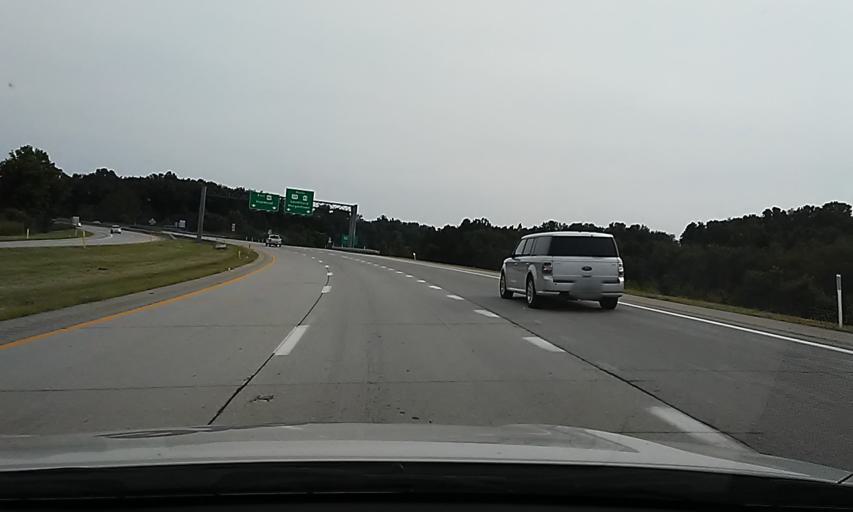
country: US
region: Pennsylvania
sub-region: Fayette County
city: Leith-Hatfield
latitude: 39.8741
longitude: -79.7455
